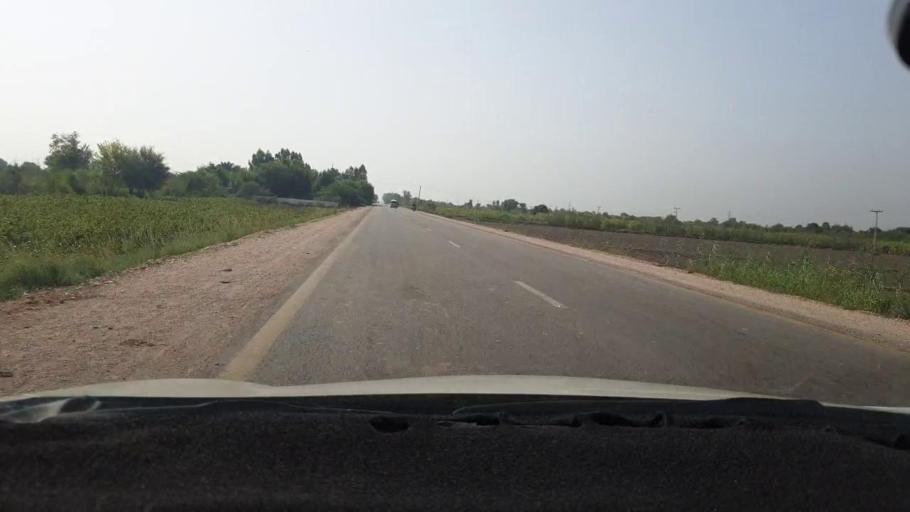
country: PK
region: Sindh
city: Sanghar
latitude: 26.0030
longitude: 68.9615
